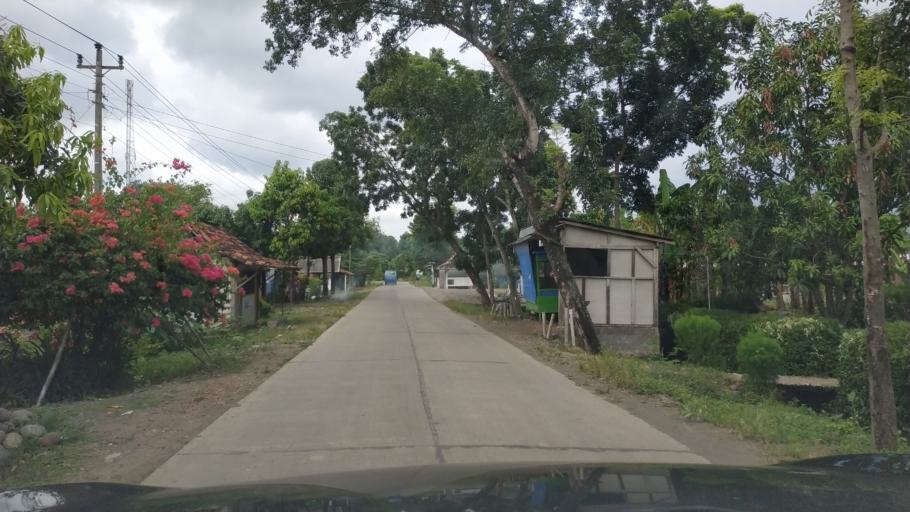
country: ID
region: Central Java
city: Pemalang
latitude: -6.9480
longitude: 109.3470
